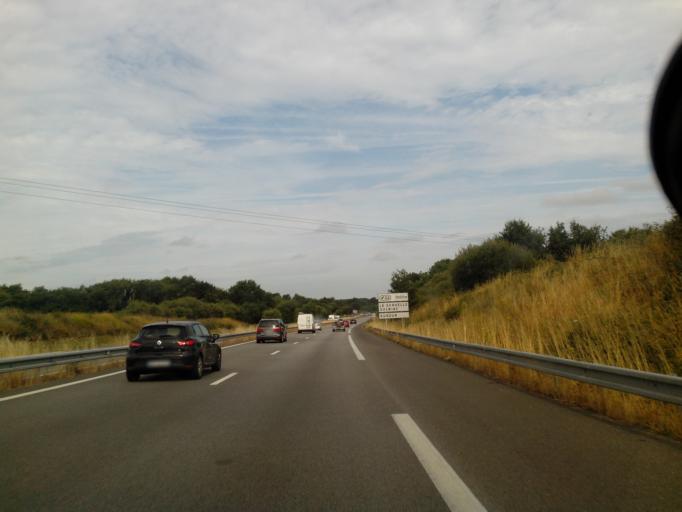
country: FR
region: Brittany
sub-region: Departement du Morbihan
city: Surzur
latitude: 47.6040
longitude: -2.5986
